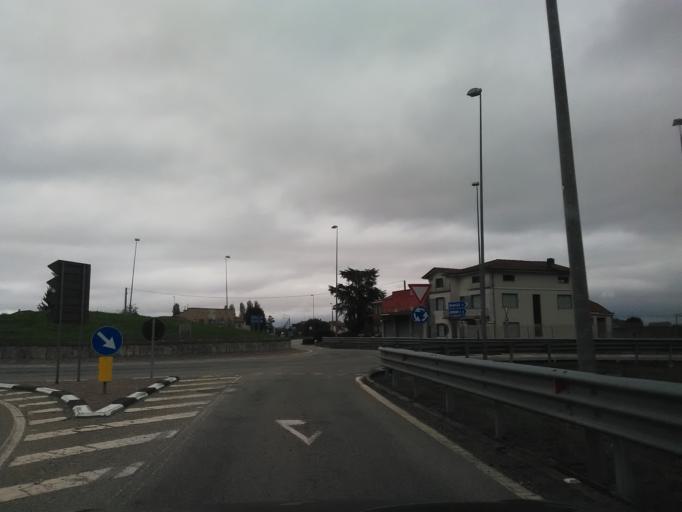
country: IT
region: Piedmont
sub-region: Provincia di Vercelli
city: Tronzano Vercellese
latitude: 45.3410
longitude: 8.1615
